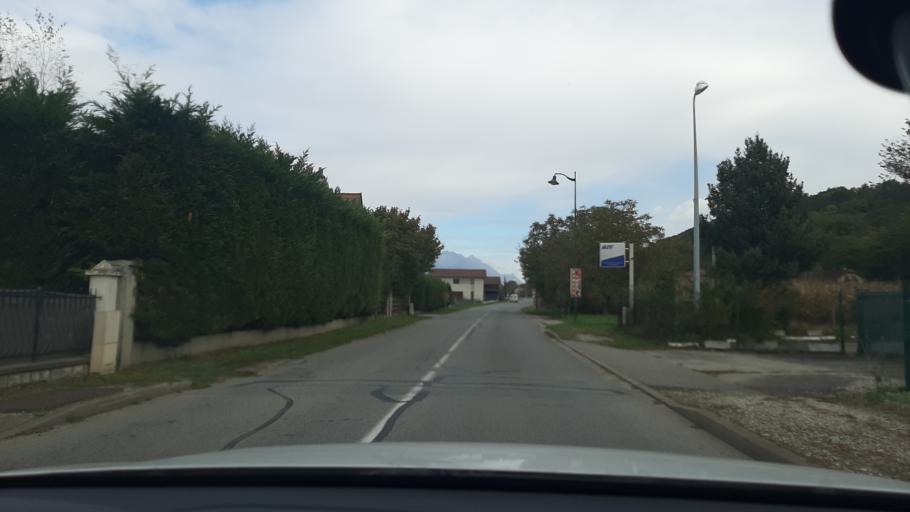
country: FR
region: Rhone-Alpes
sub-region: Departement de l'Isere
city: Pontcharra
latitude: 45.4491
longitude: 6.0395
